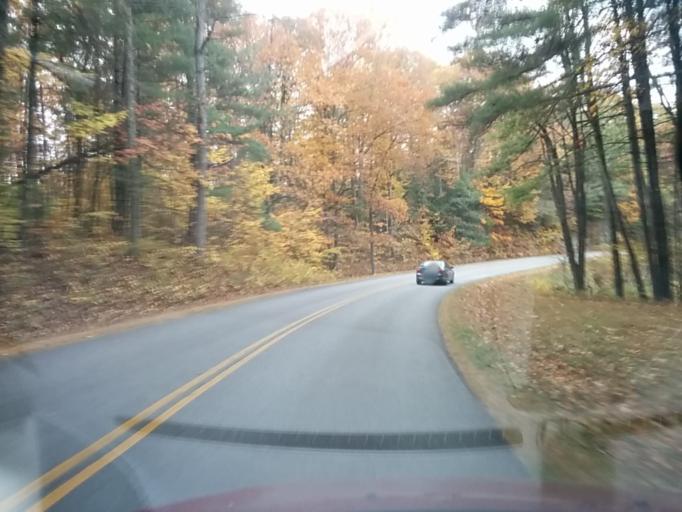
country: US
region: Virginia
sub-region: City of Buena Vista
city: Buena Vista
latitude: 37.8088
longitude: -79.2273
